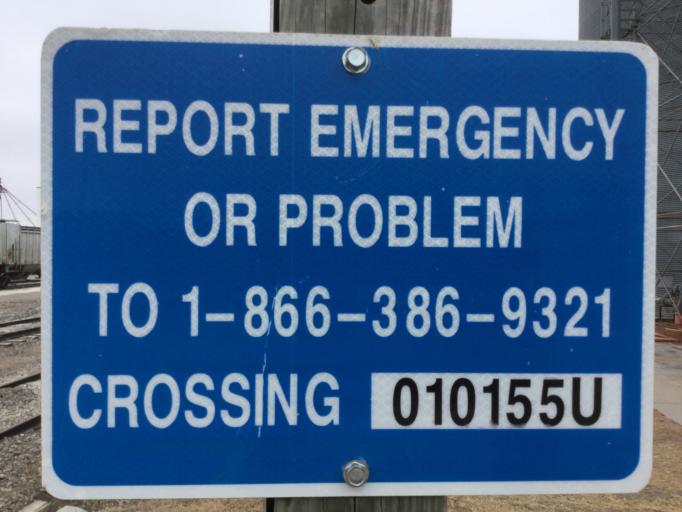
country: US
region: Kansas
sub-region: Edwards County
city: Kinsley
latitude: 38.1922
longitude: -99.5270
